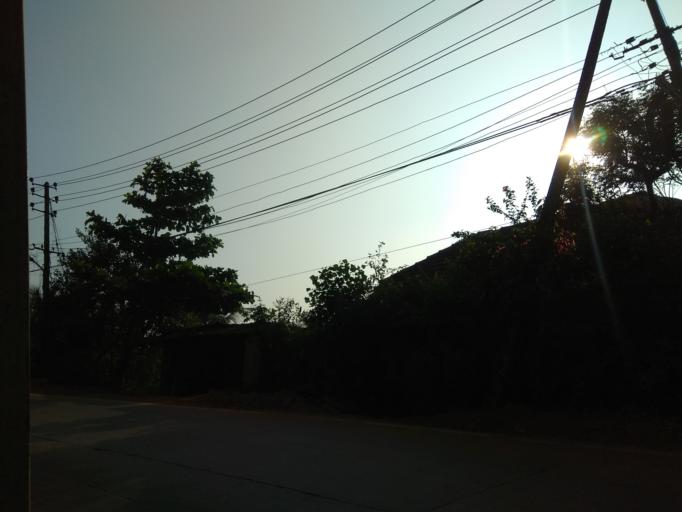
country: IN
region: Karnataka
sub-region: Dakshina Kannada
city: Mangalore
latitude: 12.9187
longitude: 74.8582
